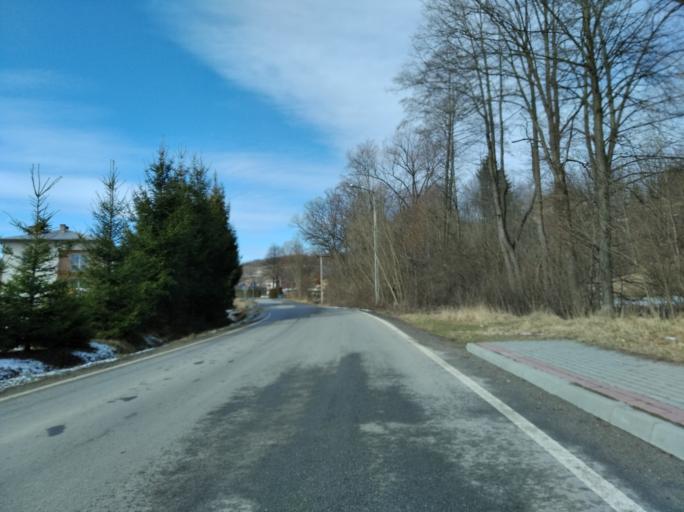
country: PL
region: Subcarpathian Voivodeship
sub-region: Powiat brzozowski
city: Jasienica Rosielna
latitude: 49.7546
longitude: 21.8955
